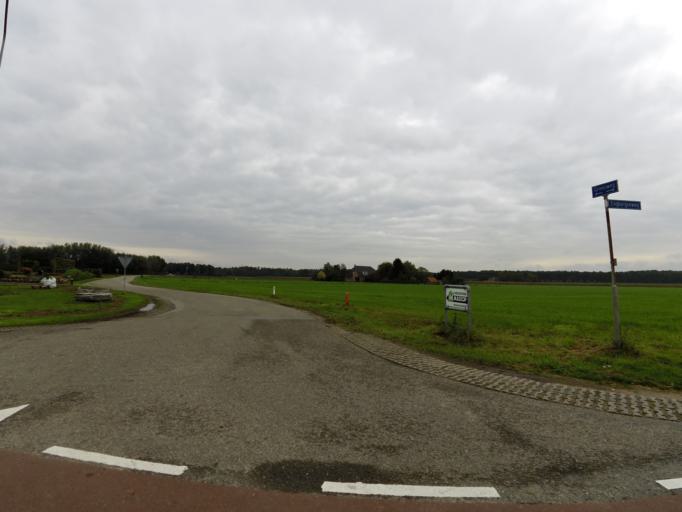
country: NL
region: Gelderland
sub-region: Oude IJsselstreek
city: Gendringen
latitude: 51.8780
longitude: 6.4083
